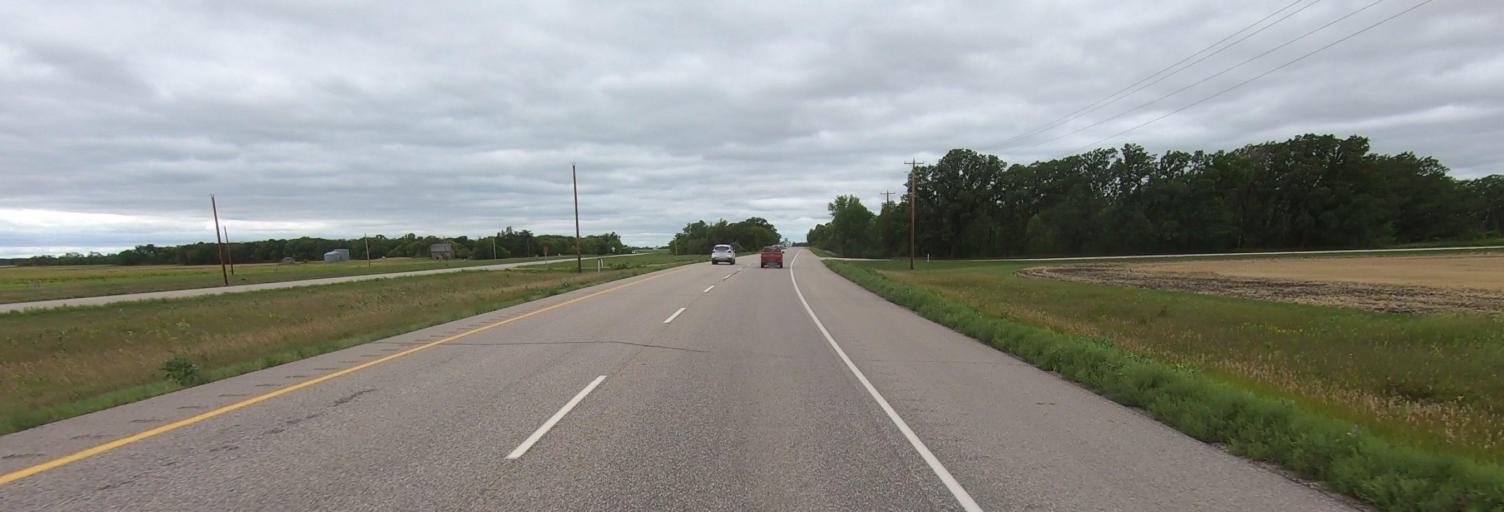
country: CA
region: Manitoba
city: Portage la Prairie
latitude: 49.9752
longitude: -98.4772
